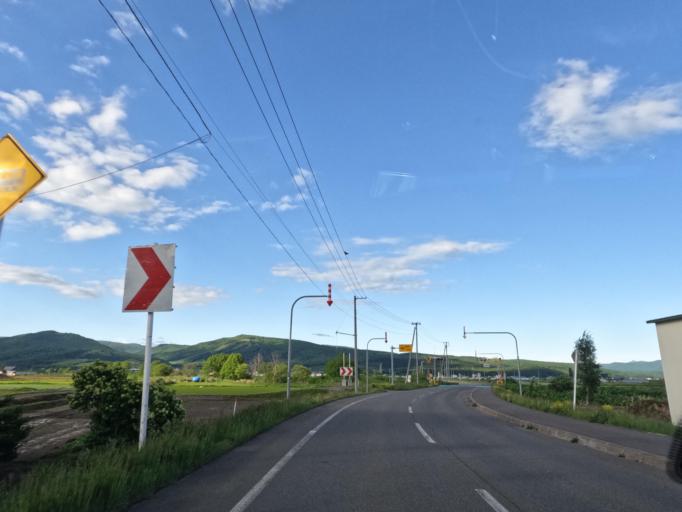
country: JP
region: Hokkaido
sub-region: Asahikawa-shi
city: Asahikawa
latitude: 43.8973
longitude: 142.4747
